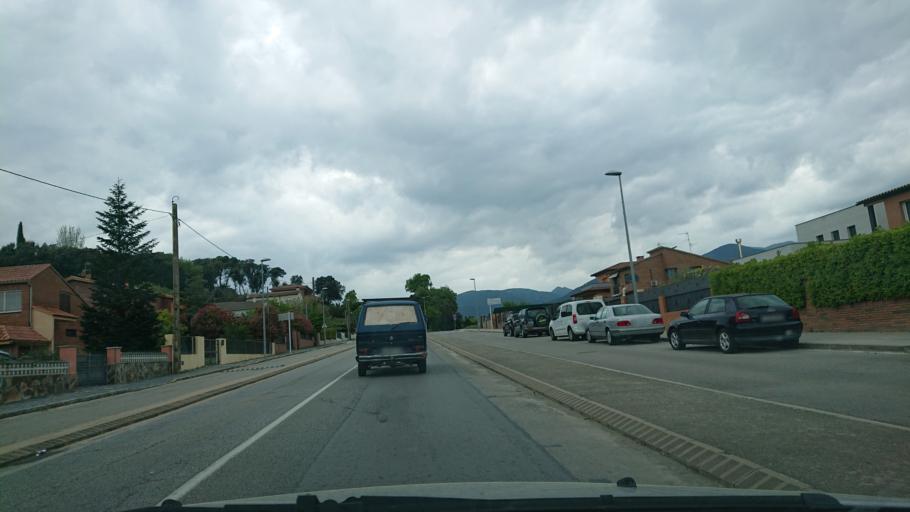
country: ES
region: Catalonia
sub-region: Provincia de Barcelona
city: Sant Pere de Vilamajor
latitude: 41.6744
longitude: 2.3950
